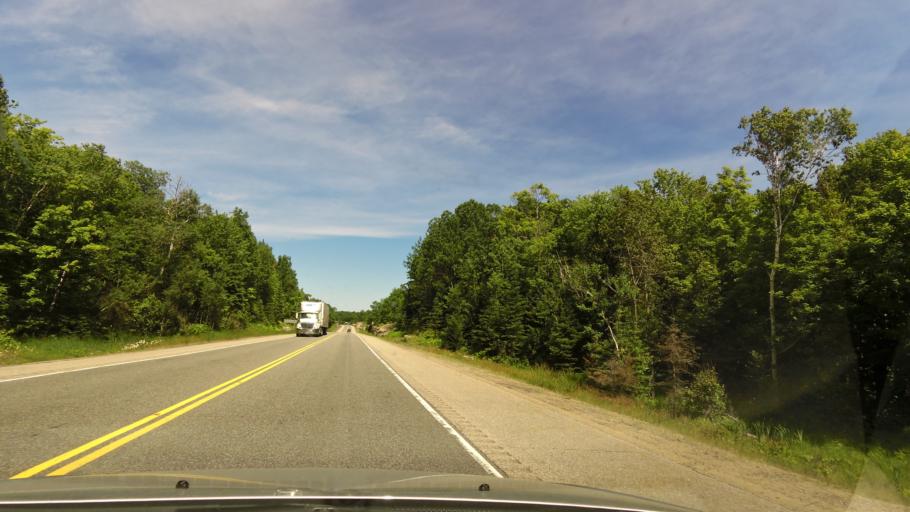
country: CA
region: Ontario
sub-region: Parry Sound District
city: Parry Sound
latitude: 45.5409
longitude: -80.2689
